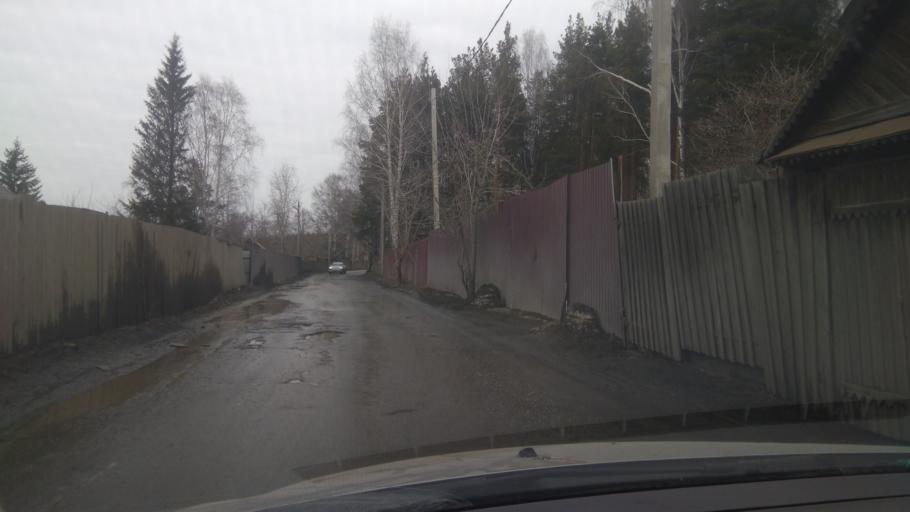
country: RU
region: Sverdlovsk
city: Severka
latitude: 56.8503
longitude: 60.3850
